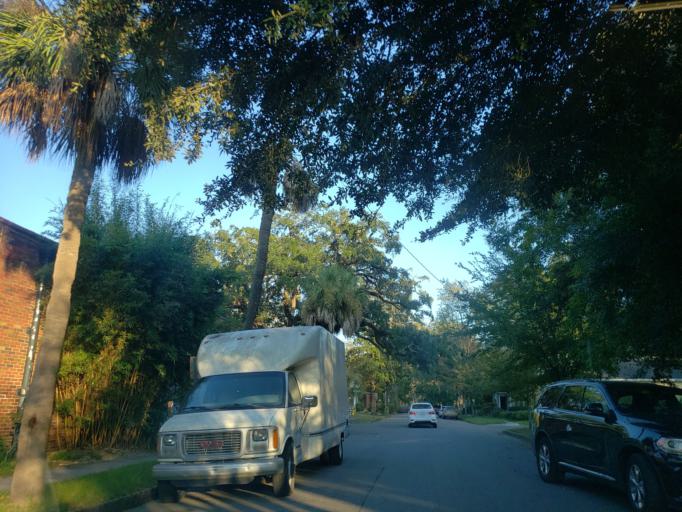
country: US
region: Georgia
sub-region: Chatham County
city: Savannah
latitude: 32.0569
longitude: -81.0915
